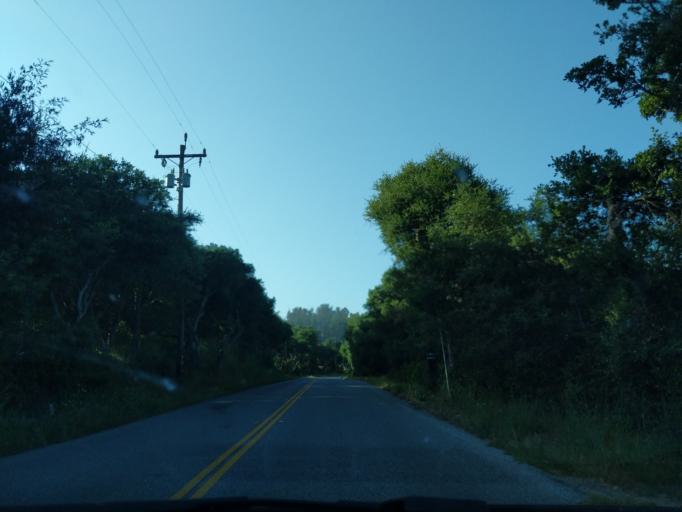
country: US
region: California
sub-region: Monterey County
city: Las Lomas
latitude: 36.8680
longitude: -121.6902
